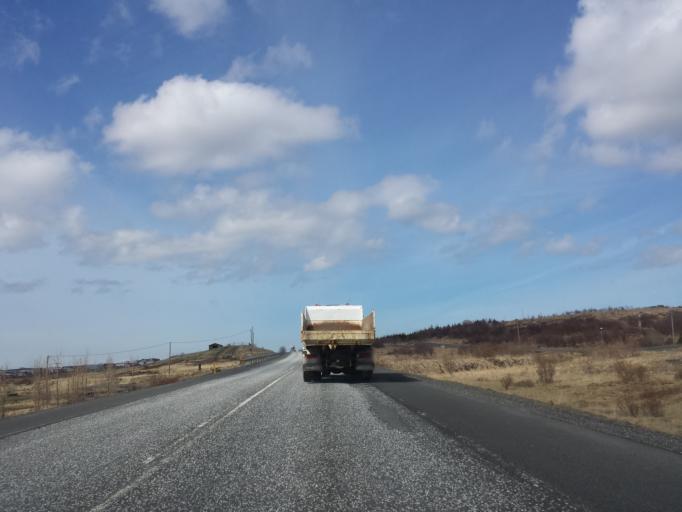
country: IS
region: Capital Region
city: Mosfellsbaer
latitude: 64.0974
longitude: -21.7429
